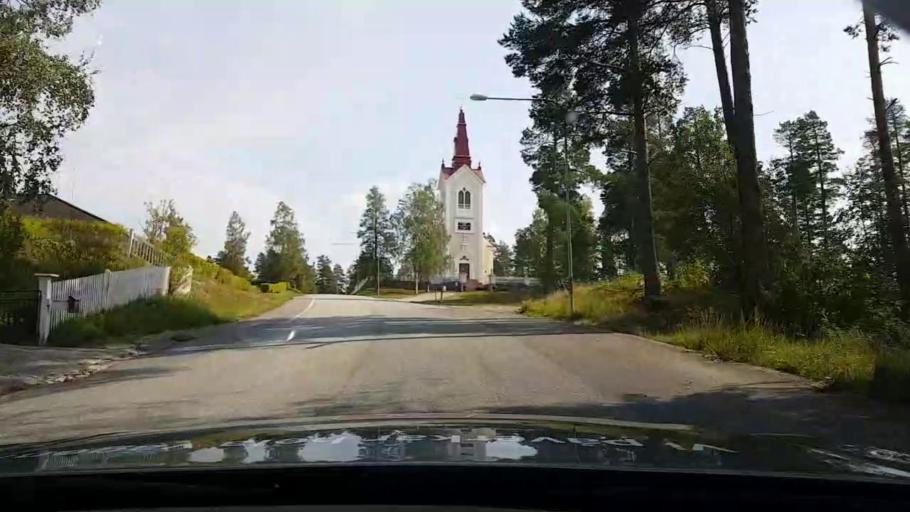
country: SE
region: Jaemtland
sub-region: Braecke Kommun
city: Braecke
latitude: 62.7444
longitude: 15.4275
